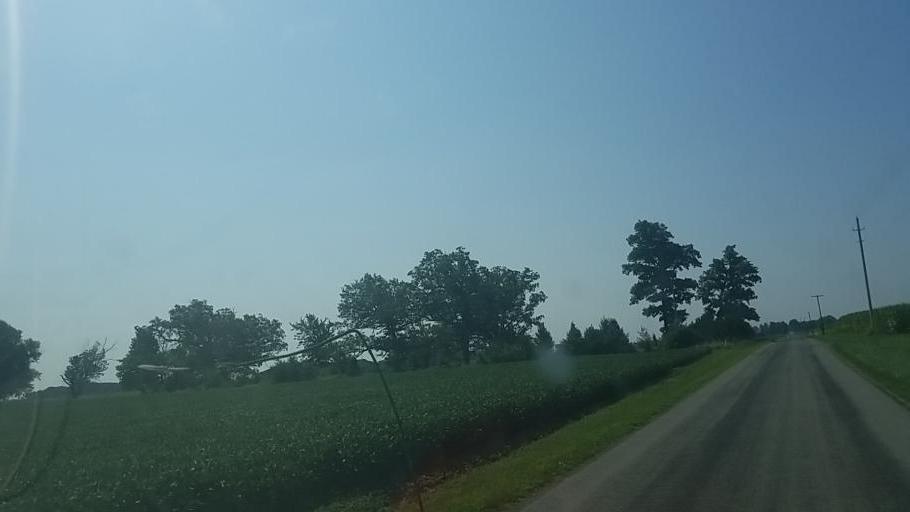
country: US
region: Ohio
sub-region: Marion County
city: Marion
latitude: 40.7135
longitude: -83.1499
